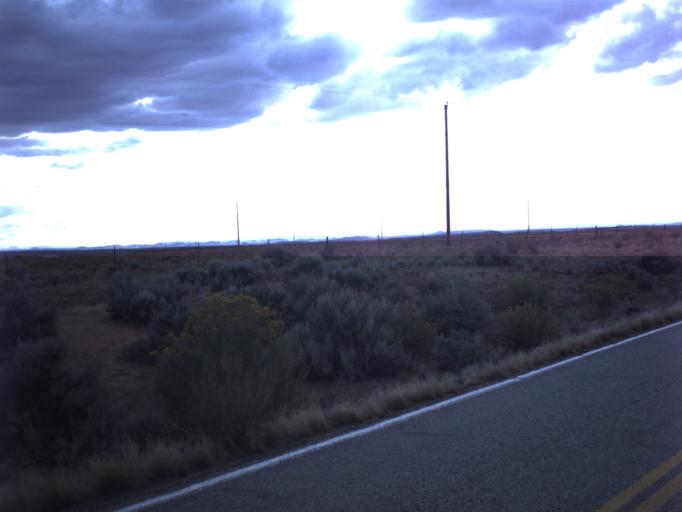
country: US
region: Utah
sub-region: San Juan County
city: Blanding
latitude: 37.4322
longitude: -109.3675
